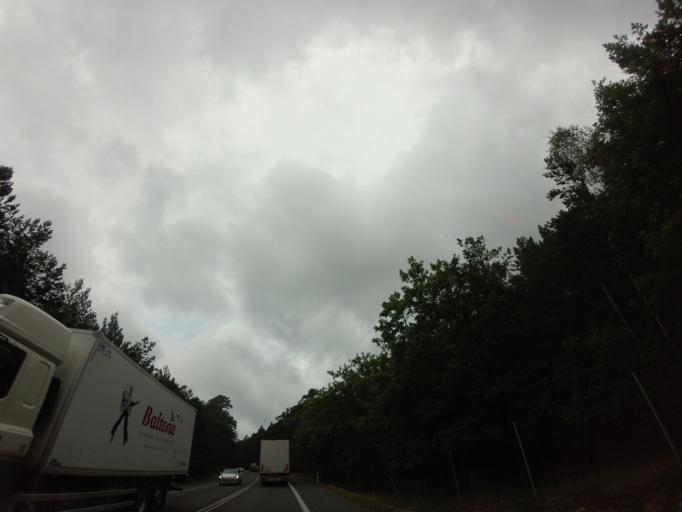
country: PL
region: West Pomeranian Voivodeship
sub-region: Powiat kamienski
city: Miedzyzdroje
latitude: 53.8895
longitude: 14.4970
